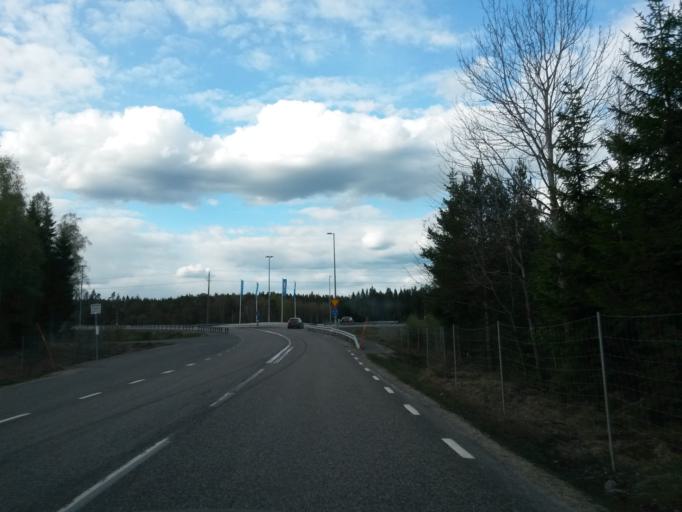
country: SE
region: Vaestra Goetaland
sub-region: Tranemo Kommun
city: Langhem
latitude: 57.6080
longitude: 13.1391
